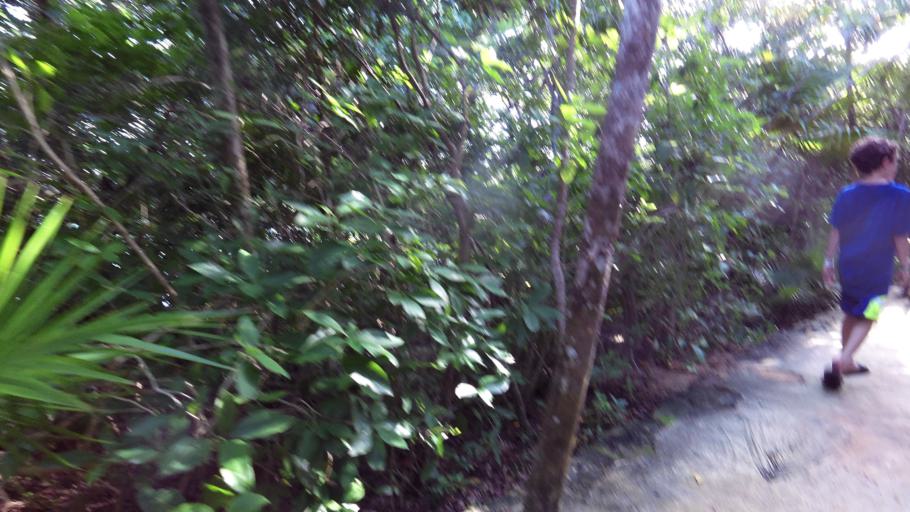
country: MX
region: Quintana Roo
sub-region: Tulum
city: Ciudad Chemuyil
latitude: 20.3193
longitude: -87.3596
